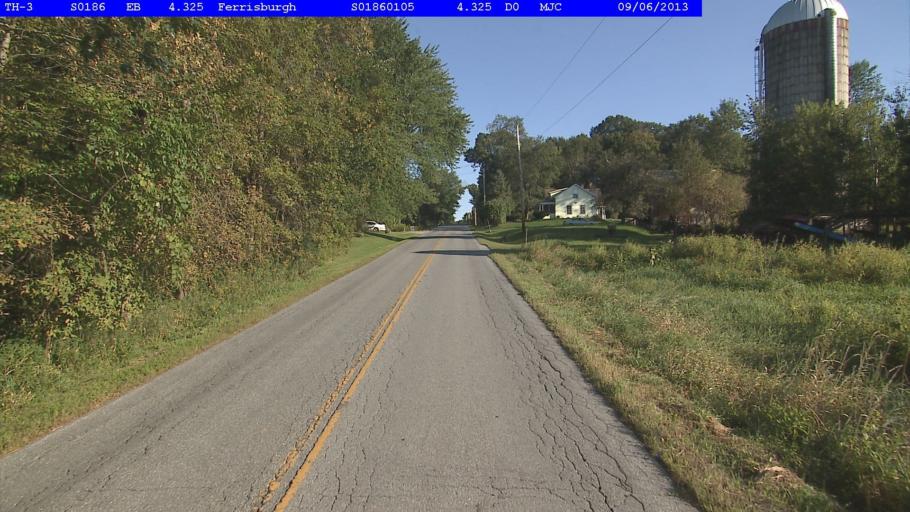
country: US
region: Vermont
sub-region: Addison County
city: Vergennes
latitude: 44.1668
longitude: -73.2976
